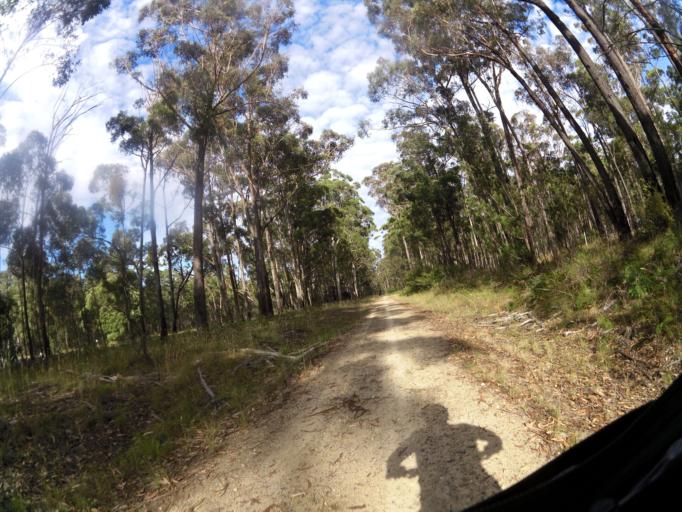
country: AU
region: Victoria
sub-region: East Gippsland
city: Lakes Entrance
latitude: -37.7451
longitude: 148.3941
